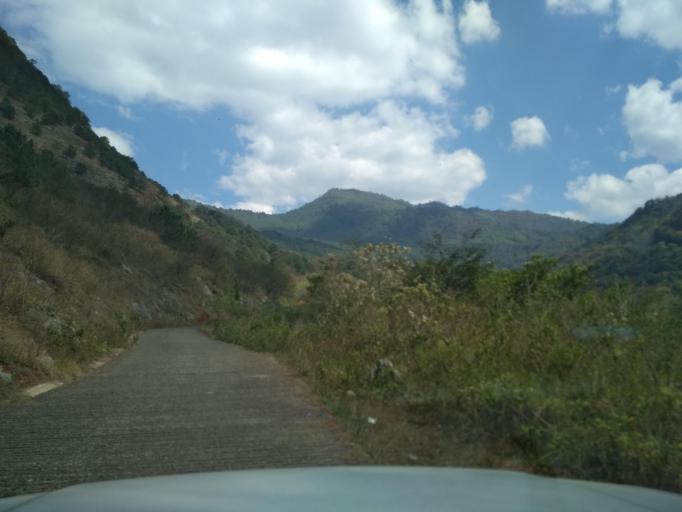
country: MX
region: Veracruz
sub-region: Tlilapan
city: Tonalixco
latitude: 18.7878
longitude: -97.0873
